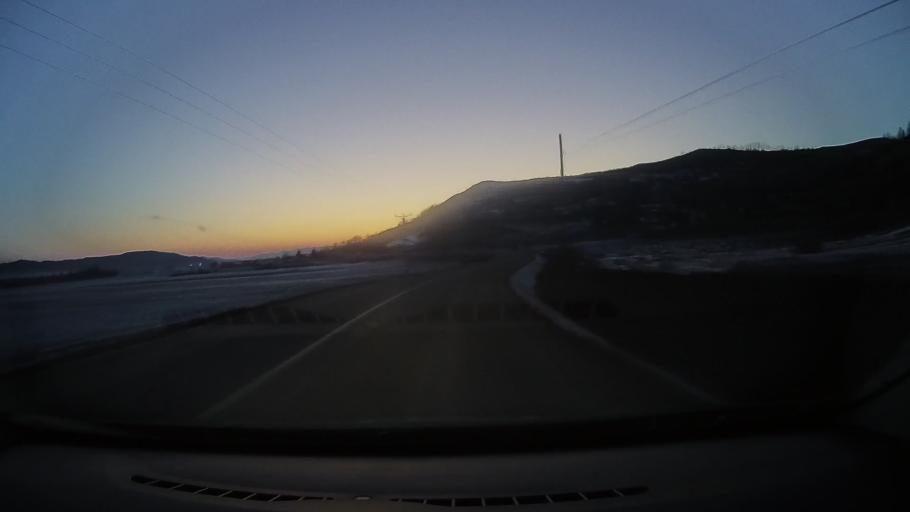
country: RO
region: Sibiu
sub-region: Comuna Brateiu
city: Brateiu
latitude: 46.1921
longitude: 24.4285
